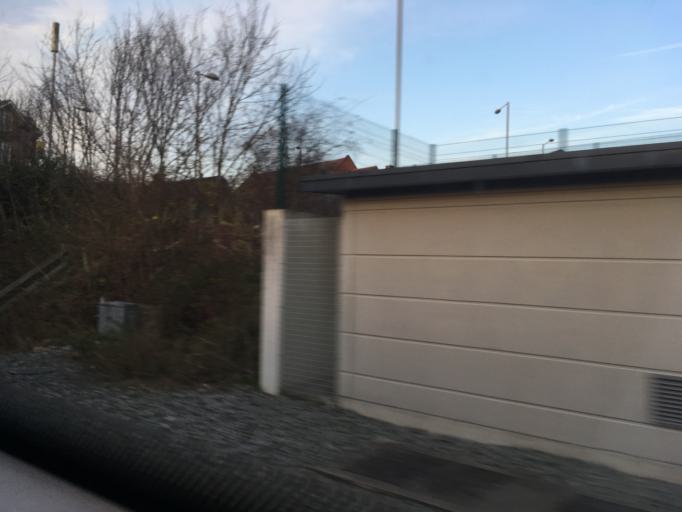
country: GB
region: England
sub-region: Manchester
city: Didsbury
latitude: 53.4169
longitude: -2.2288
